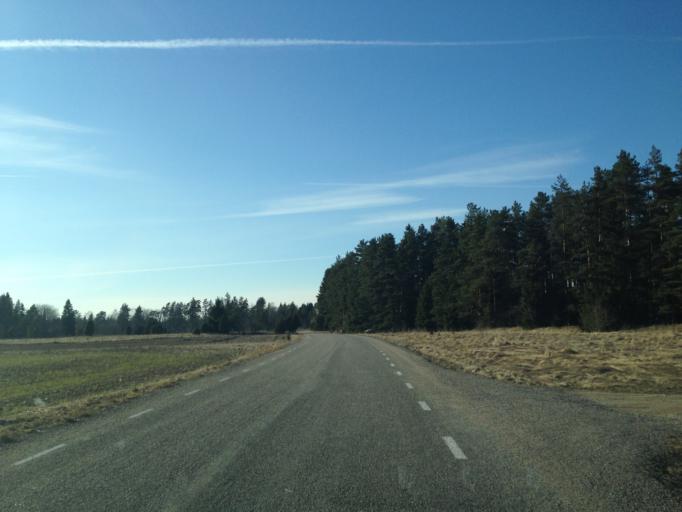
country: EE
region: Harju
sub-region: Nissi vald
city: Turba
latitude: 59.1406
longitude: 24.1651
